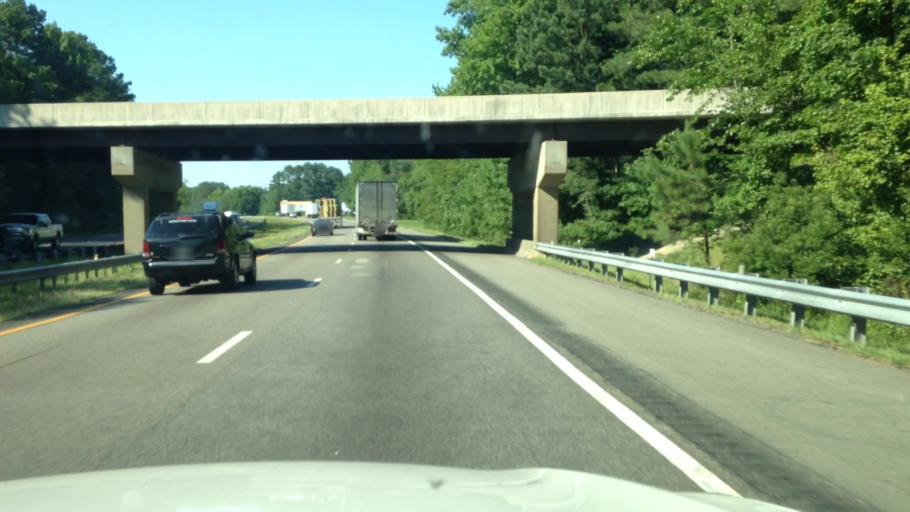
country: US
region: Virginia
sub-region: City of Petersburg
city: Petersburg
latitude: 37.0813
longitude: -77.3583
